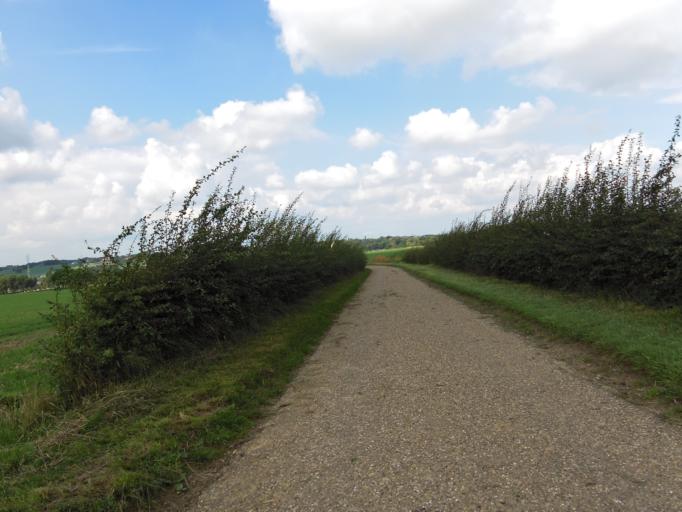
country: NL
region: Limburg
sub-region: Gemeente Voerendaal
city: Klimmen
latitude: 50.8590
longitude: 5.9023
